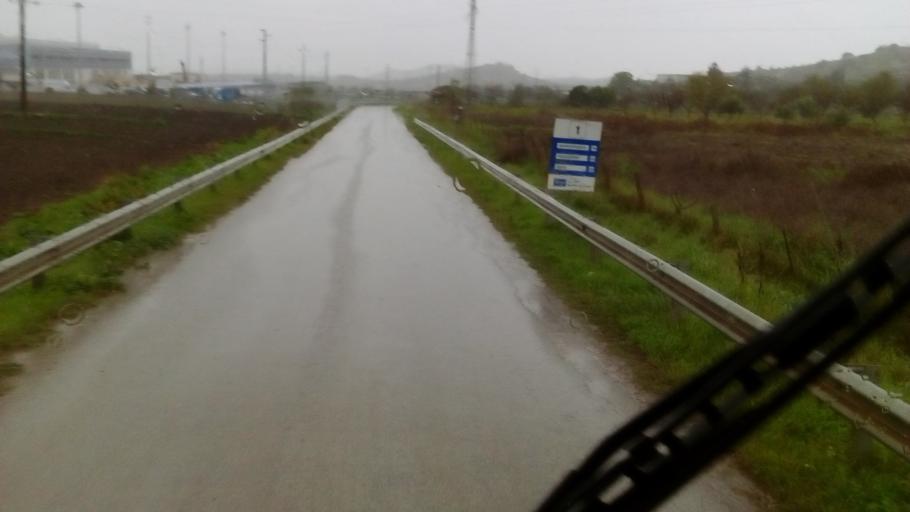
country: IT
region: Sicily
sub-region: Enna
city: Pietraperzia
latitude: 37.4061
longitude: 14.1419
